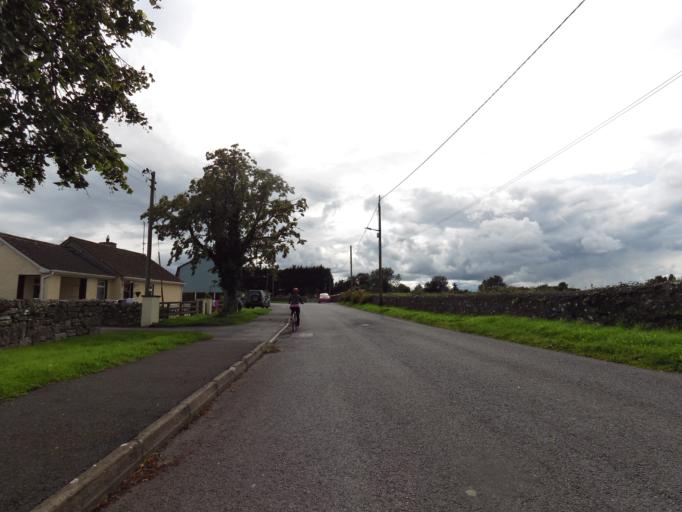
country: IE
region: Leinster
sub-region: An Longfort
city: Edgeworthstown
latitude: 53.5833
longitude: -7.5392
